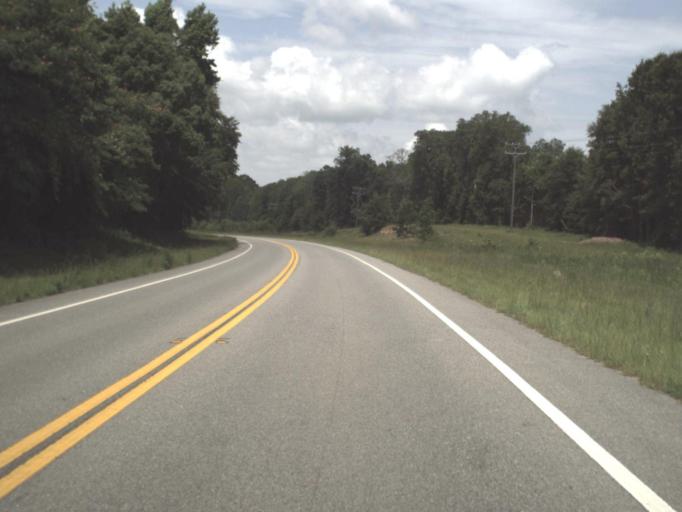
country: US
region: Florida
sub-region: Madison County
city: Madison
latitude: 30.4725
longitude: -83.6067
